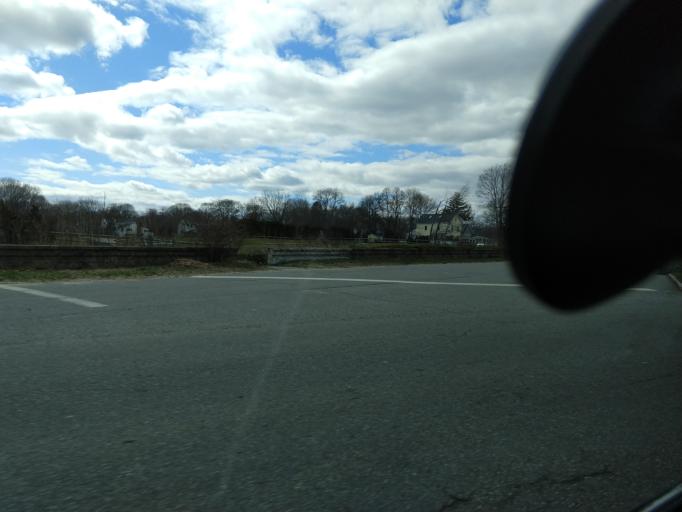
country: US
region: Massachusetts
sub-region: Essex County
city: Newburyport
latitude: 42.8028
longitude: -70.8534
